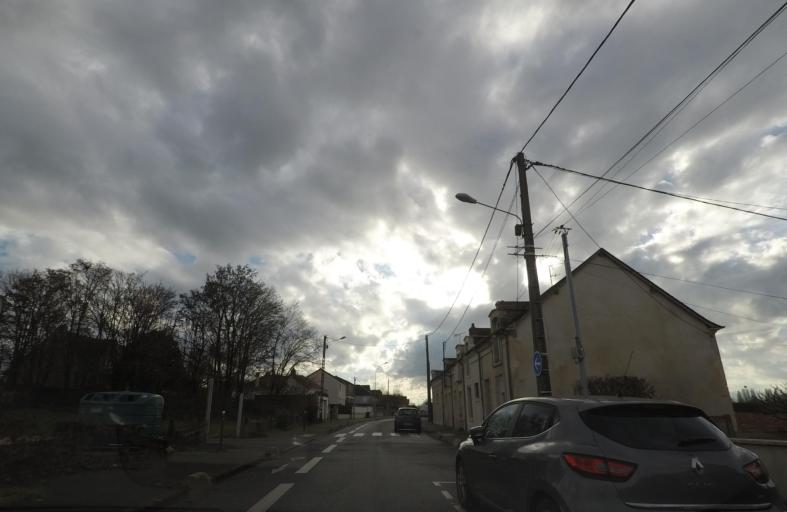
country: FR
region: Centre
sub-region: Departement du Cher
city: Bourges
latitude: 47.0664
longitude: 2.3994
